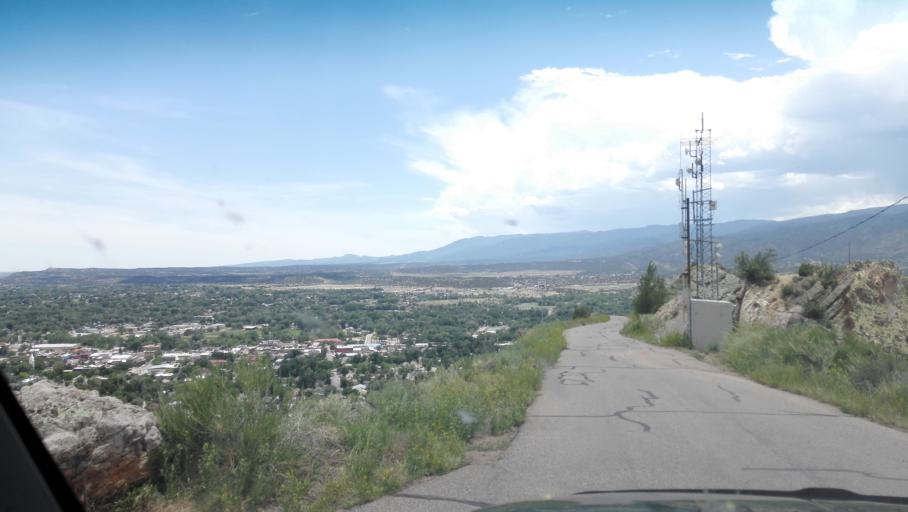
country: US
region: Colorado
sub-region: Fremont County
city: Canon City
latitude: 38.4498
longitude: -105.2492
